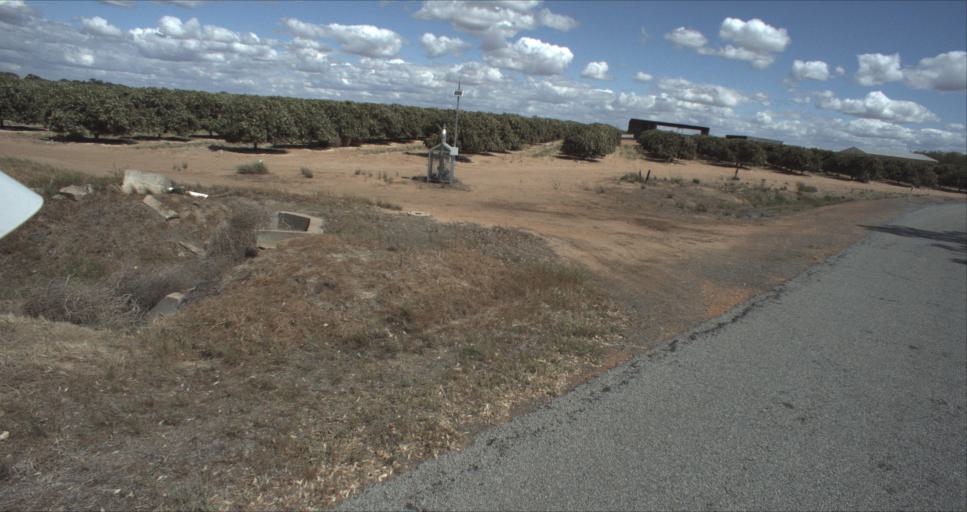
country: AU
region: New South Wales
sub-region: Leeton
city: Leeton
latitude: -34.5176
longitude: 146.2285
